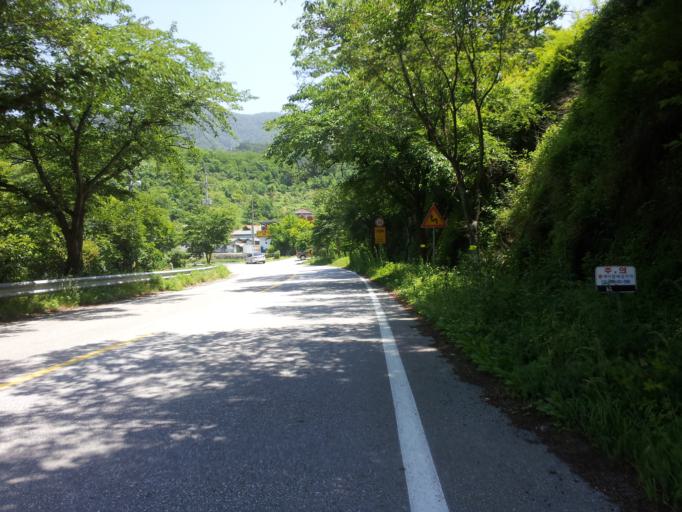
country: KR
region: Chungcheongbuk-do
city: Okcheon
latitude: 36.3556
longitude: 127.5949
